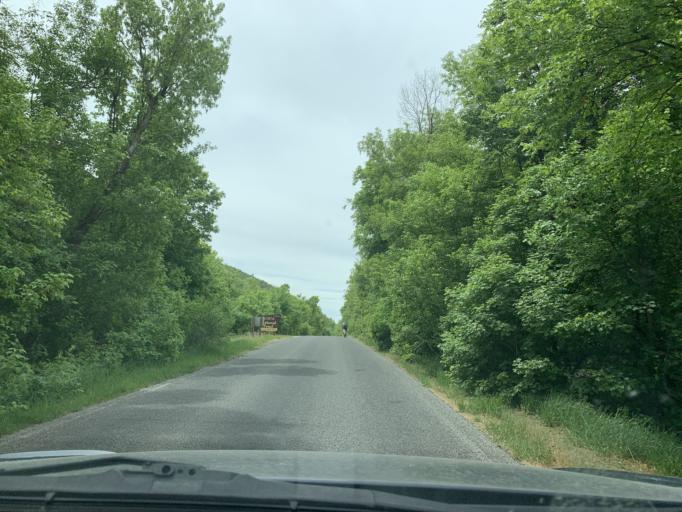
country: US
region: Utah
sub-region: Utah County
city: Mapleton
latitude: 40.1686
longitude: -111.4795
